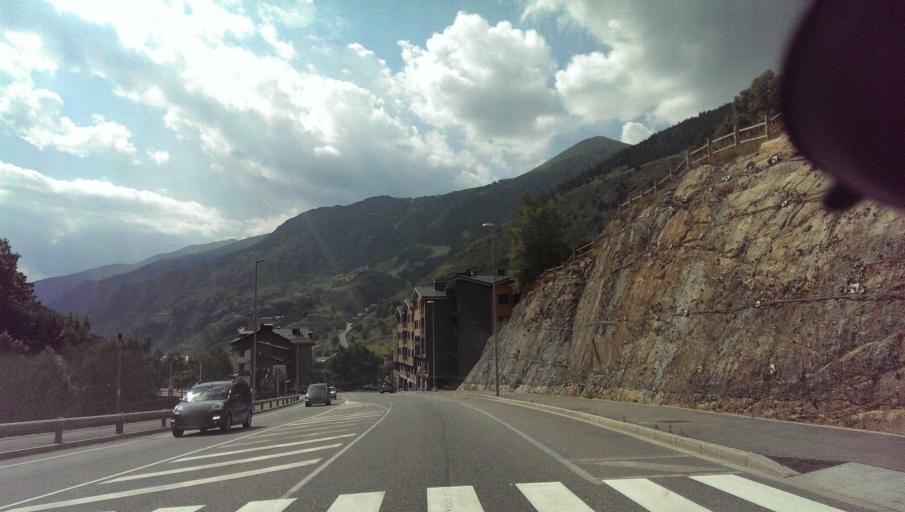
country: AD
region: Canillo
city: El Tarter
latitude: 42.5784
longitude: 1.6519
